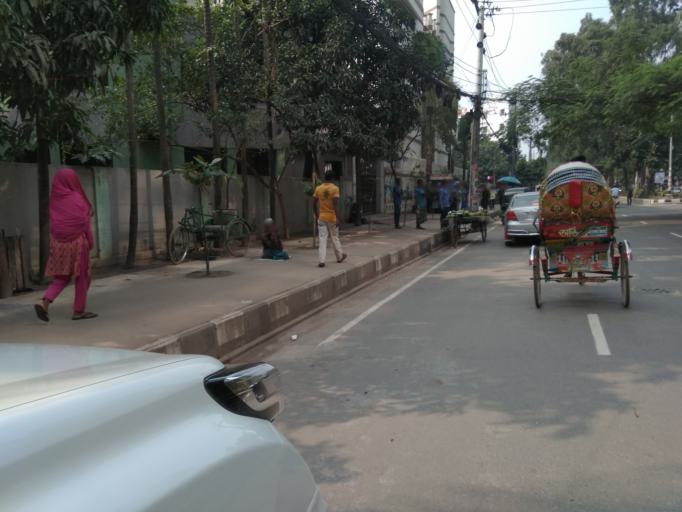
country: BD
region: Dhaka
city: Tungi
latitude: 23.8607
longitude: 90.3990
